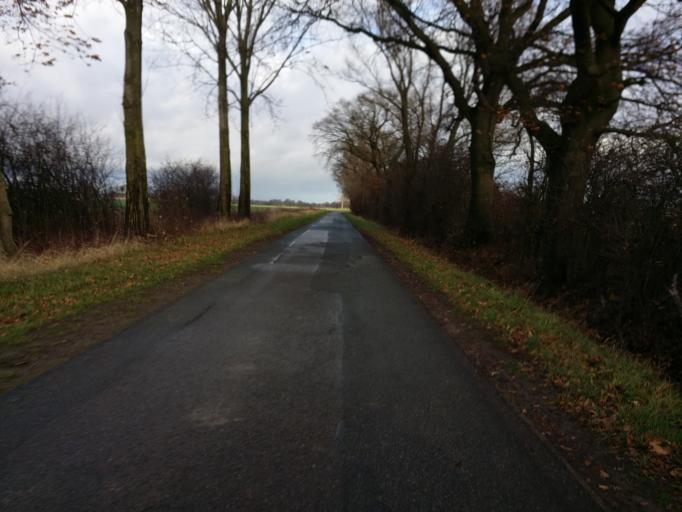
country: DE
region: Lower Saxony
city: Riede
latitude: 52.9835
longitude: 8.9758
